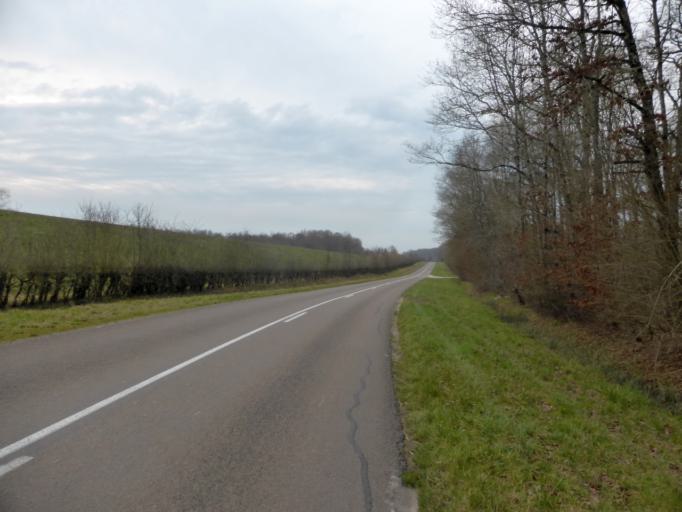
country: FR
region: Champagne-Ardenne
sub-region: Departement de l'Aube
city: Lusigny-sur-Barse
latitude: 48.2712
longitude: 4.3009
